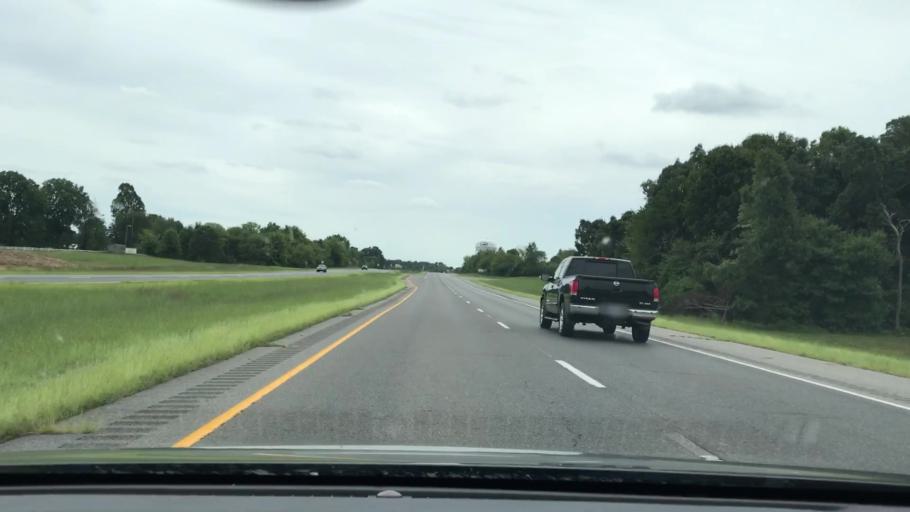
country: US
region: Kentucky
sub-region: Marshall County
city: Benton
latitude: 36.8342
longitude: -88.3754
